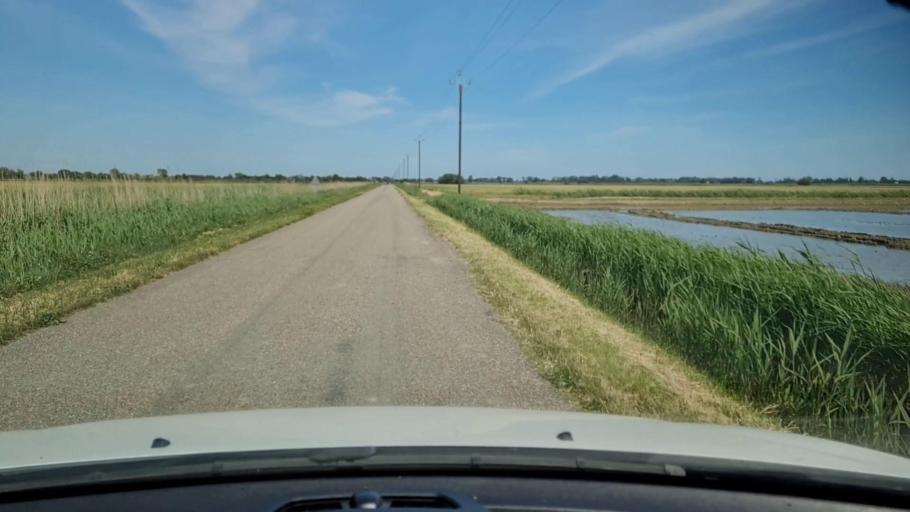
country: FR
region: Languedoc-Roussillon
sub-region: Departement du Gard
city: Saint-Gilles
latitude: 43.6027
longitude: 4.4385
